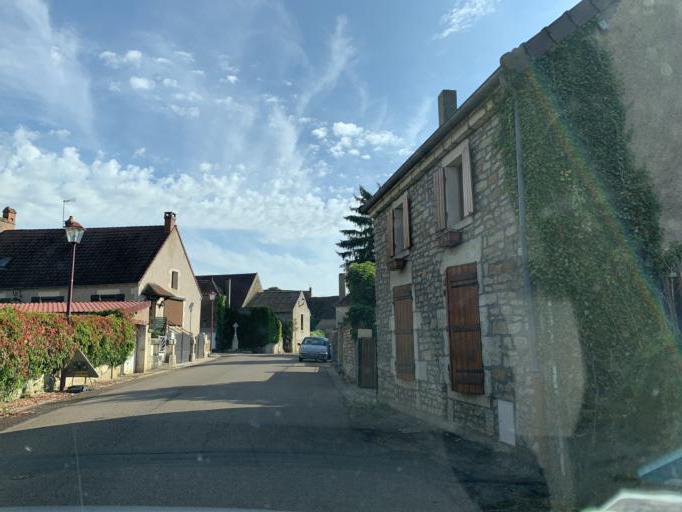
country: FR
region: Bourgogne
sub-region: Departement de la Nievre
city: Varzy
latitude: 47.4461
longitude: 3.4132
